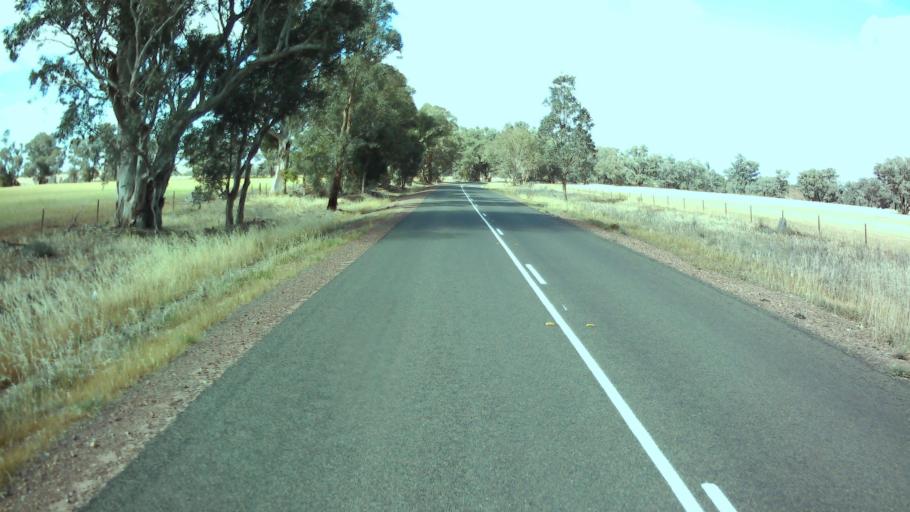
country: AU
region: New South Wales
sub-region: Weddin
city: Grenfell
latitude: -33.9835
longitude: 148.4163
